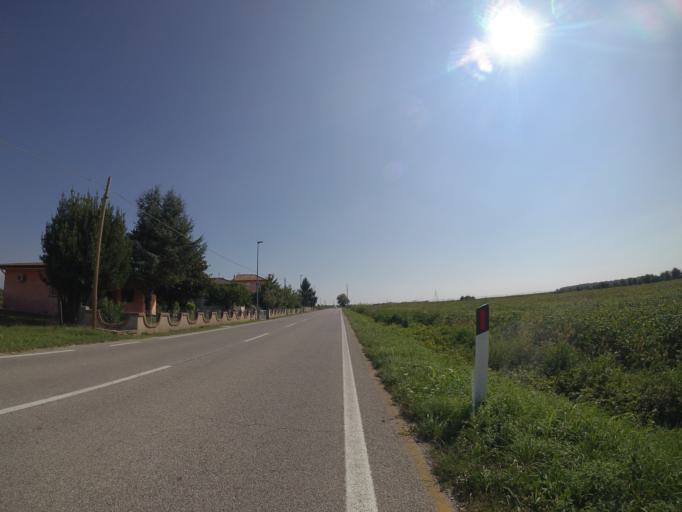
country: IT
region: Friuli Venezia Giulia
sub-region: Provincia di Udine
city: Carlino
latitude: 45.8041
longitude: 13.1656
